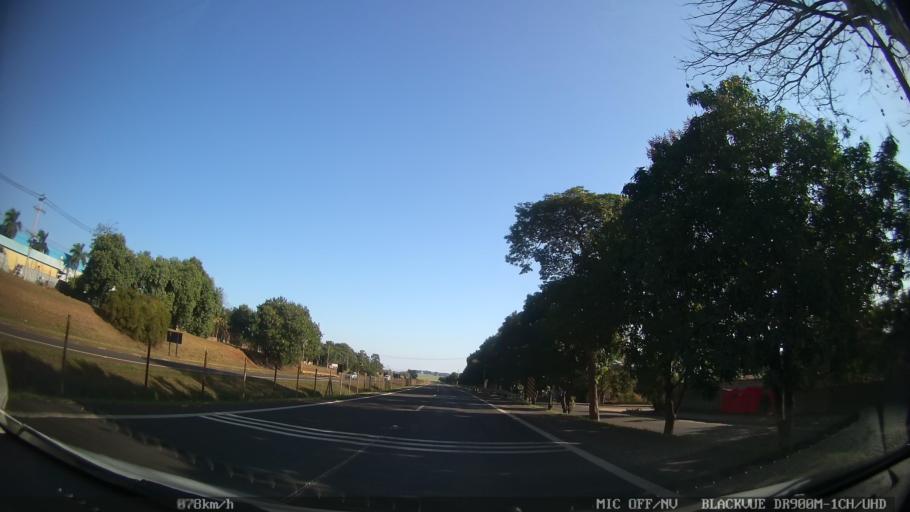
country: BR
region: Sao Paulo
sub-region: Piracicaba
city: Piracicaba
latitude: -22.6699
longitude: -47.6259
